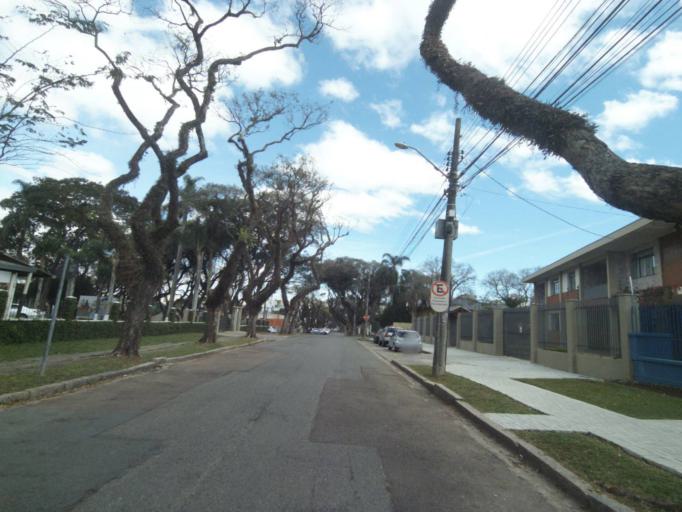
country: BR
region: Parana
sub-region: Curitiba
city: Curitiba
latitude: -25.4688
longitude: -49.2839
